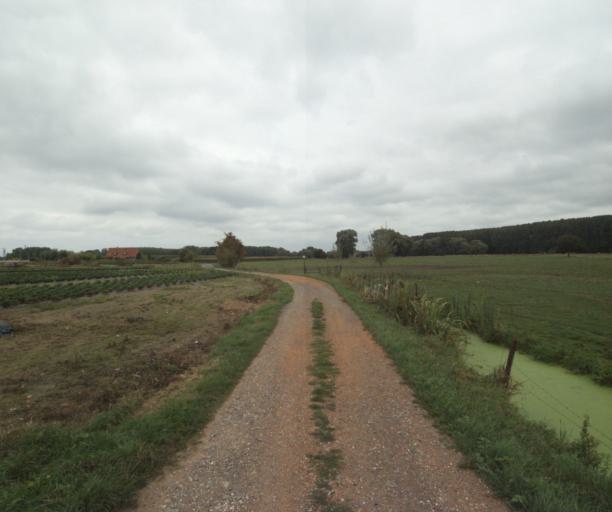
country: FR
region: Nord-Pas-de-Calais
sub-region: Departement du Nord
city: Tressin
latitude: 50.6275
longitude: 3.2022
